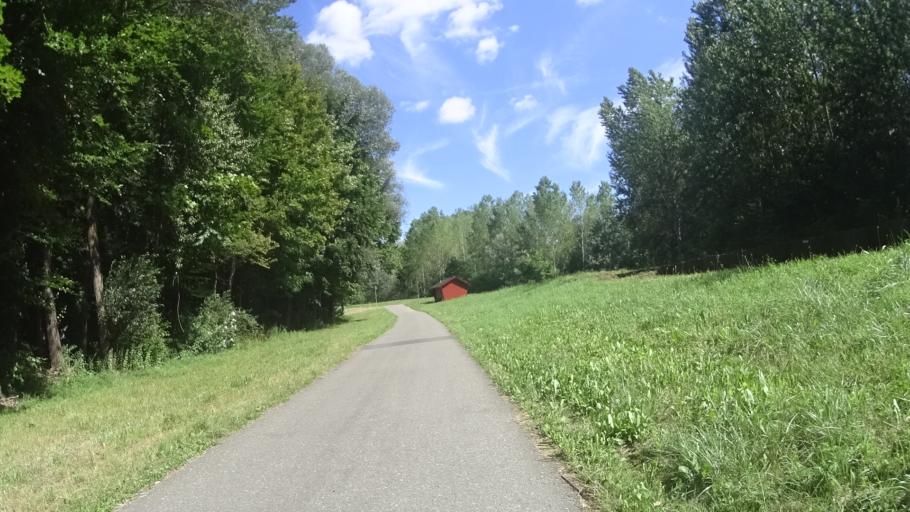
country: DE
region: Rheinland-Pfalz
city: Leimersheim
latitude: 49.1646
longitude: 8.3632
